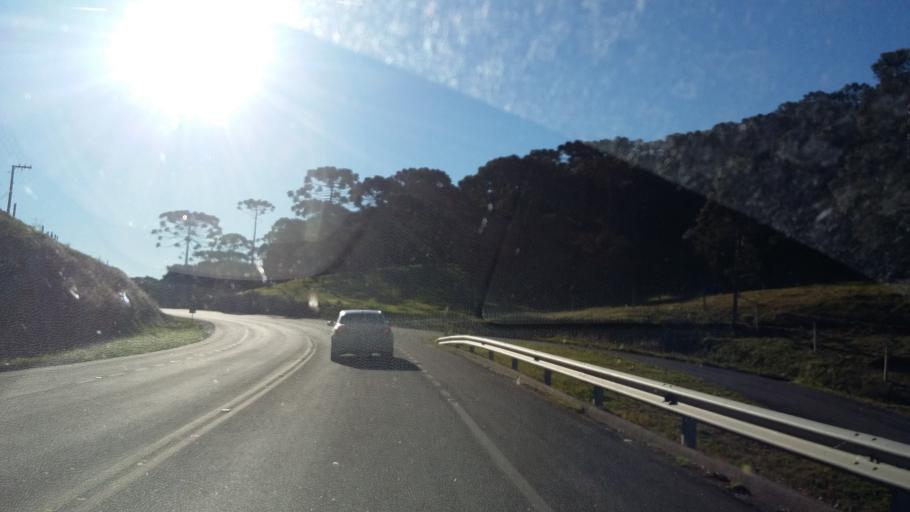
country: BR
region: Santa Catarina
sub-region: Lauro Muller
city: Lauro Muller
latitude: -28.0040
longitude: -49.5422
